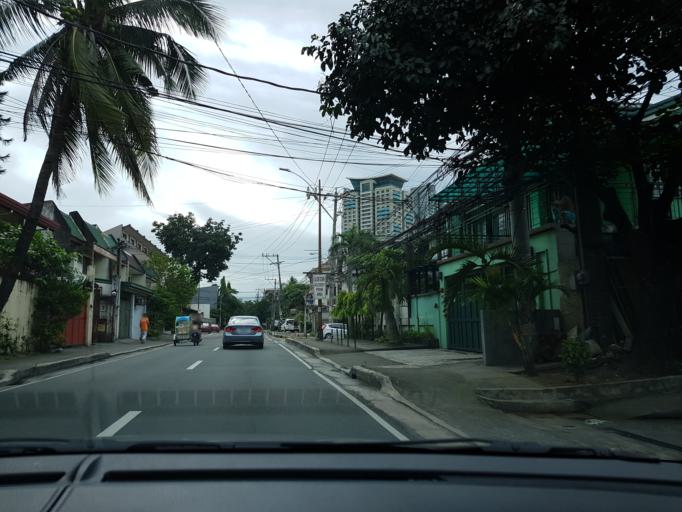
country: PH
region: Metro Manila
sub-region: San Juan
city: San Juan
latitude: 14.6194
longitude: 121.0381
